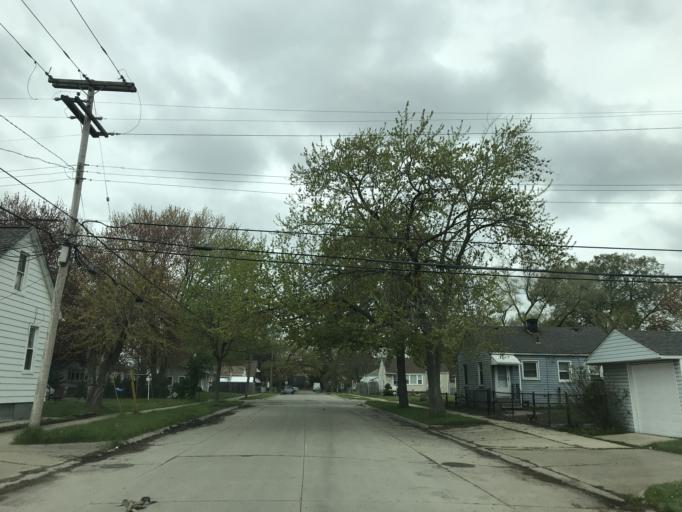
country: US
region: Michigan
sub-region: Wayne County
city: Melvindale
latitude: 42.2866
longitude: -83.1866
